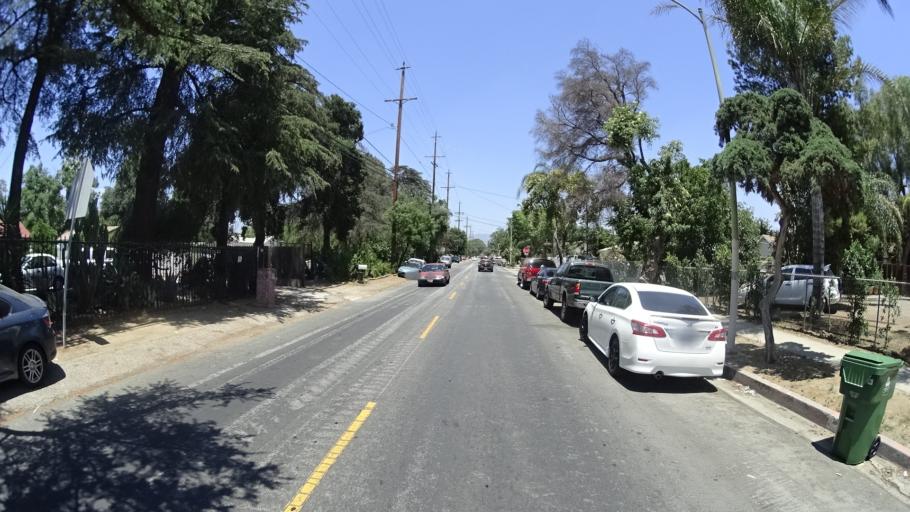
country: US
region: California
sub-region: Los Angeles County
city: Van Nuys
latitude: 34.2324
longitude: -118.4611
